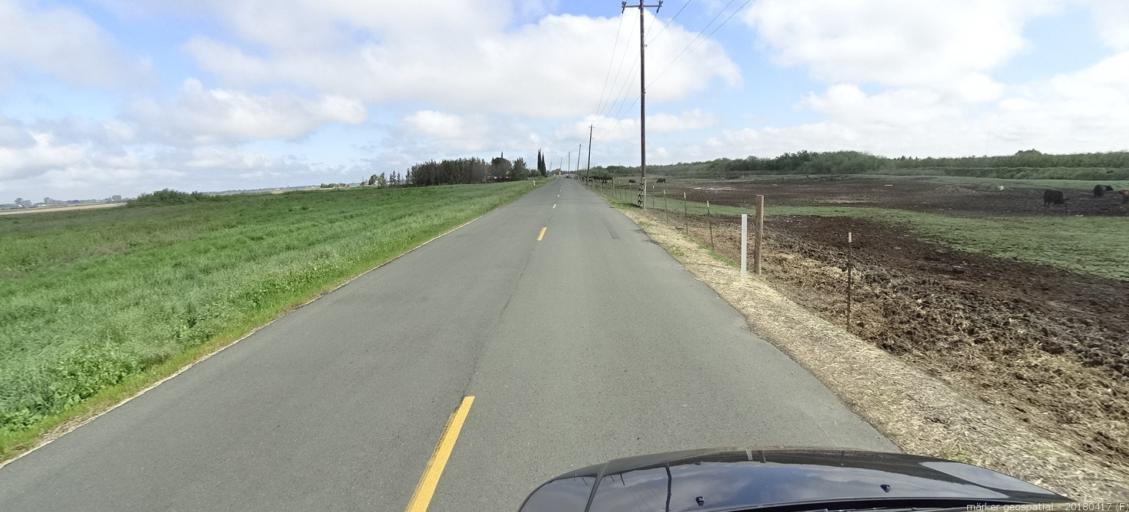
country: US
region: California
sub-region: Sacramento County
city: Walnut Grove
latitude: 38.2413
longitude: -121.5654
